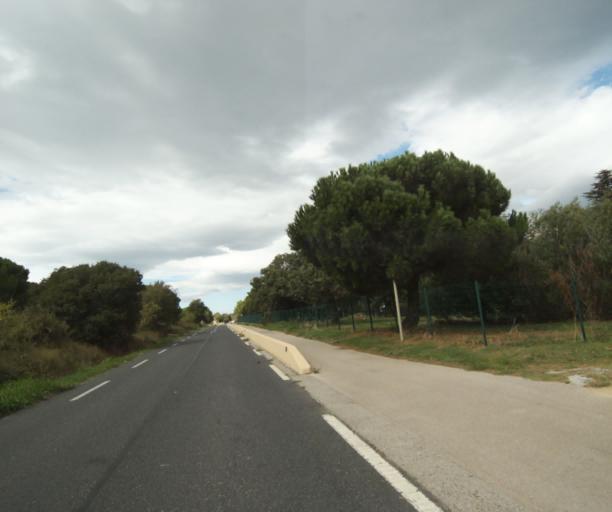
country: FR
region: Languedoc-Roussillon
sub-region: Departement des Pyrenees-Orientales
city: Argelers
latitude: 42.5387
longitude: 3.0398
